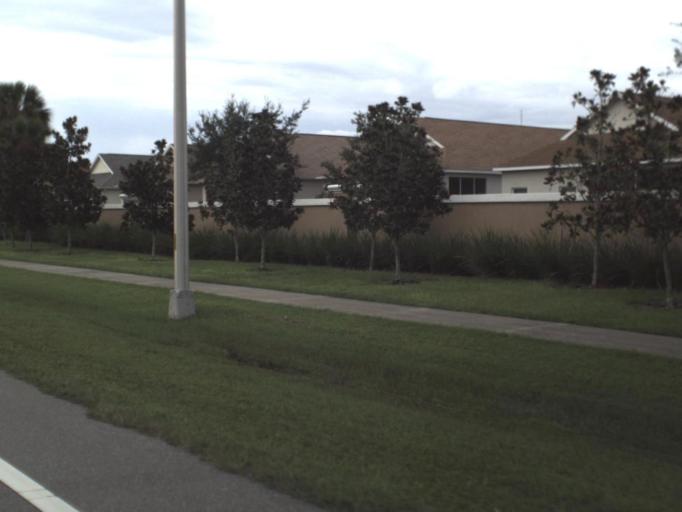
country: US
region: Florida
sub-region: Sarasota County
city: Venice Gardens
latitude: 27.0997
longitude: -82.3937
